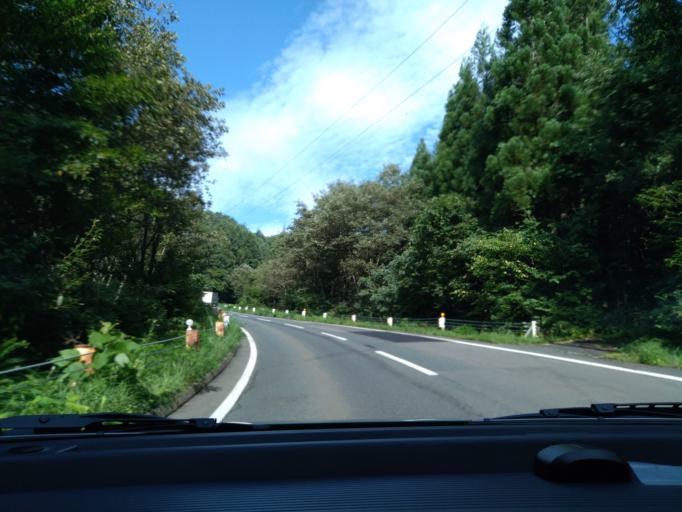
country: JP
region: Iwate
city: Shizukuishi
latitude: 39.6385
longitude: 141.0105
